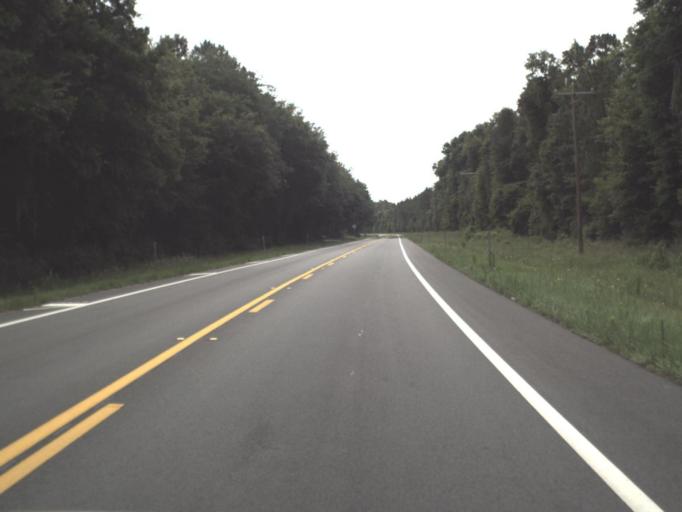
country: US
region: Florida
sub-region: Jefferson County
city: Monticello
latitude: 30.4895
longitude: -83.7069
